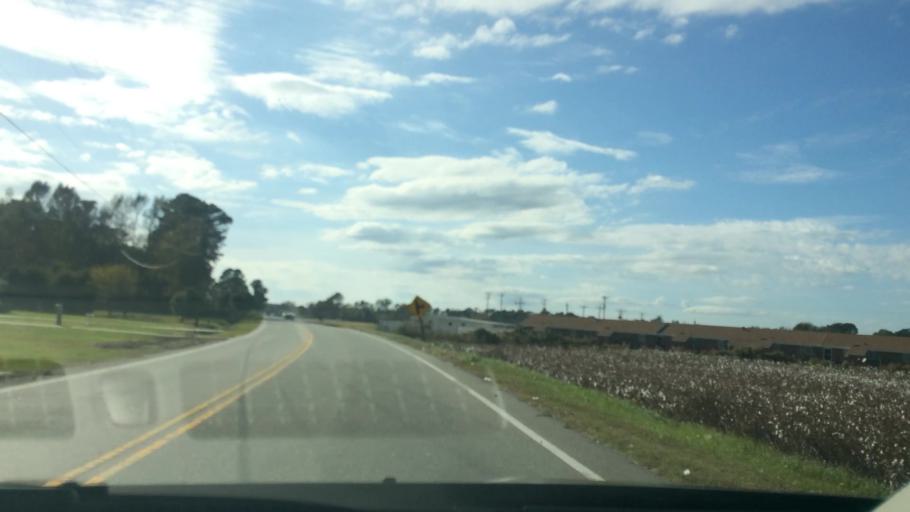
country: US
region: North Carolina
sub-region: Wayne County
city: Elroy
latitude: 35.4417
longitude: -77.8446
